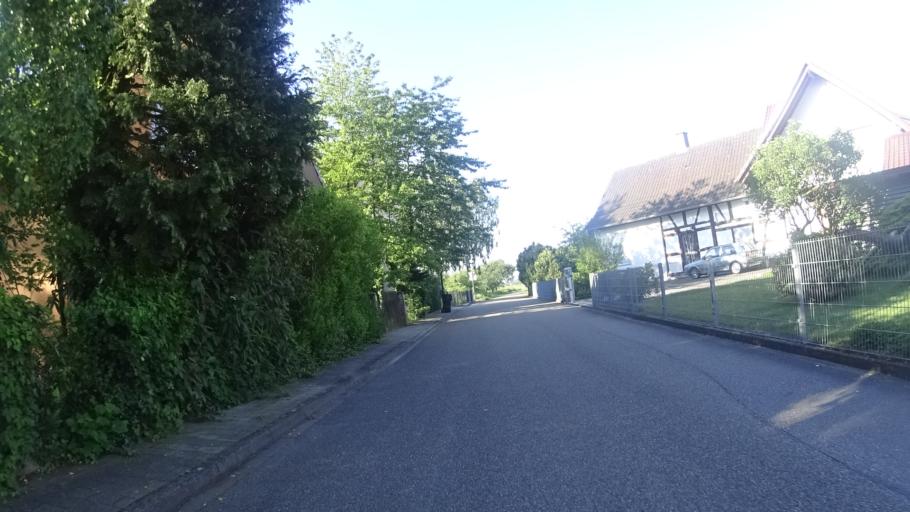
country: DE
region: Baden-Wuerttemberg
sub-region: Freiburg Region
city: Rheinau
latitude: 48.6667
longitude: 7.9295
